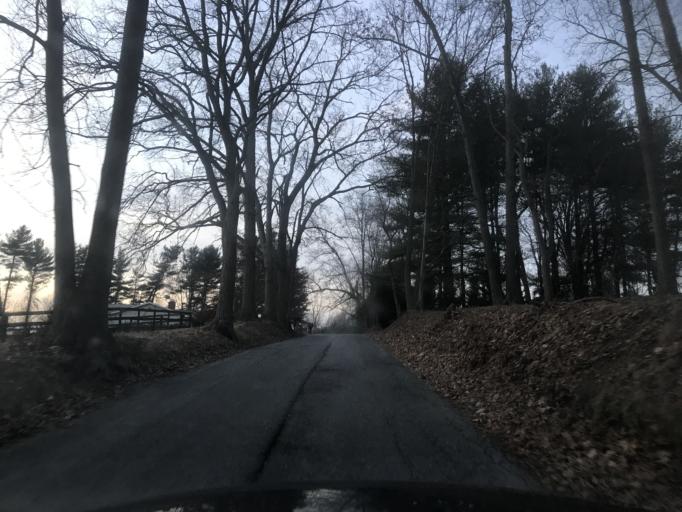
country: US
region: Pennsylvania
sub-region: York County
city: New Freedom
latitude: 39.6761
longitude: -76.7060
